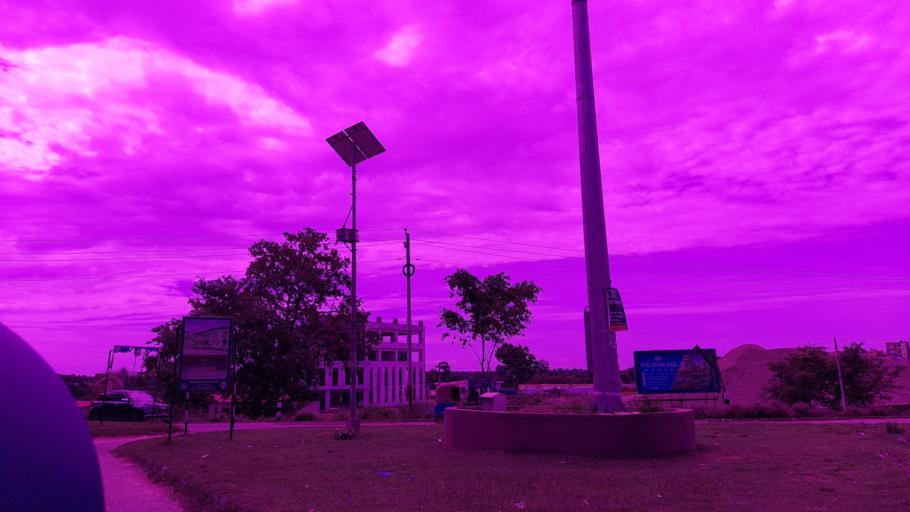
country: NP
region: Mid Western
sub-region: Bheri Zone
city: Nepalgunj
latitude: 28.1990
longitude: 81.6913
